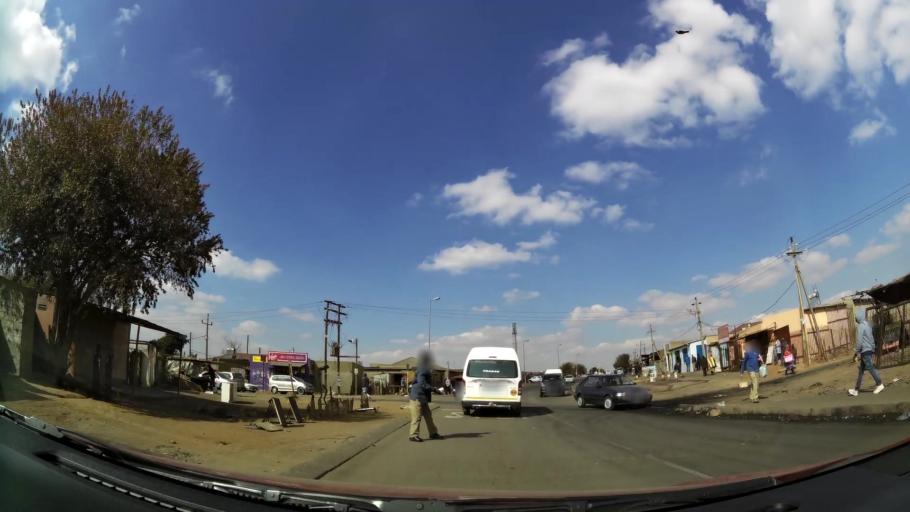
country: ZA
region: Gauteng
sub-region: Ekurhuleni Metropolitan Municipality
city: Tembisa
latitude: -25.9939
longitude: 28.2028
